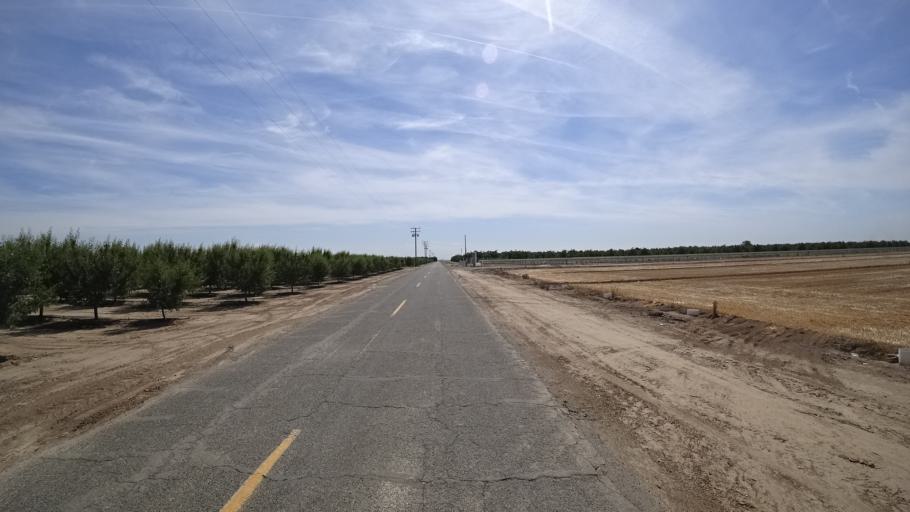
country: US
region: California
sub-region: Kings County
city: Hanford
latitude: 36.3575
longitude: -119.5535
